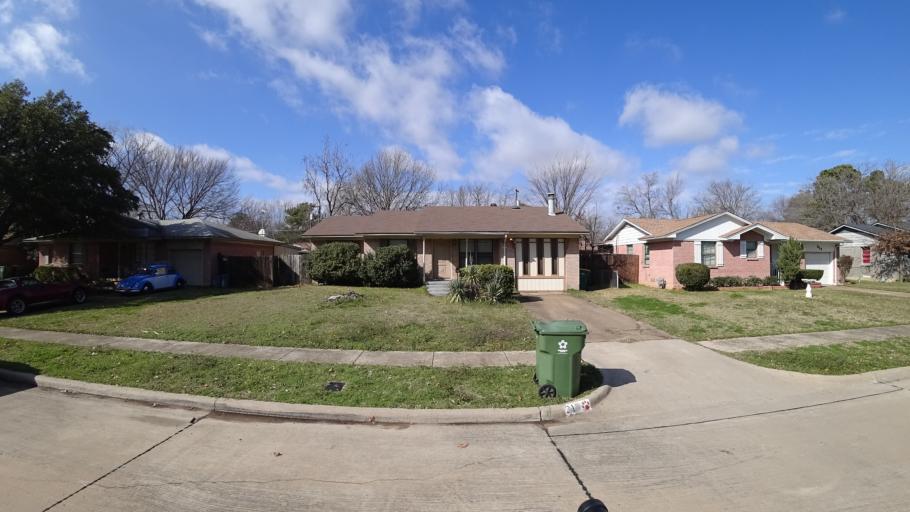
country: US
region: Texas
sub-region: Denton County
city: Lewisville
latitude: 33.0334
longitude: -96.9991
